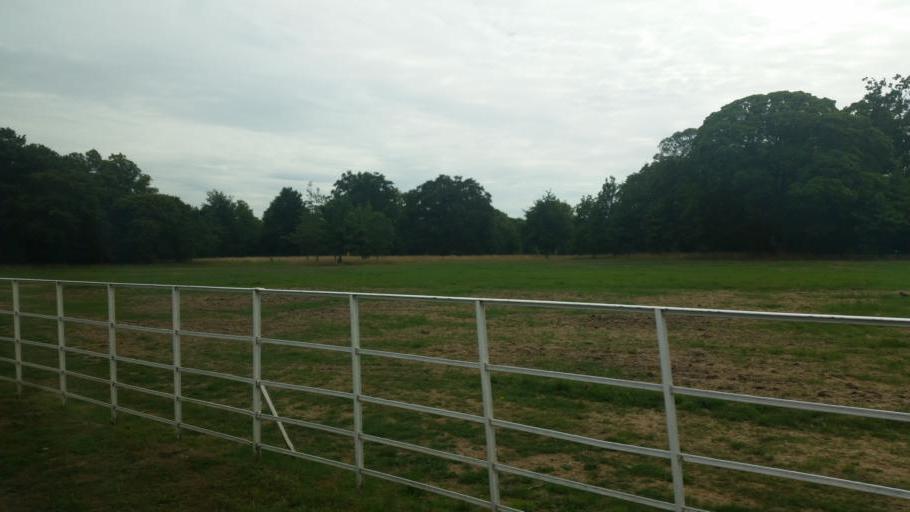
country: IE
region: Leinster
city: Chapelizod
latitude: 53.3641
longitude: -6.3302
